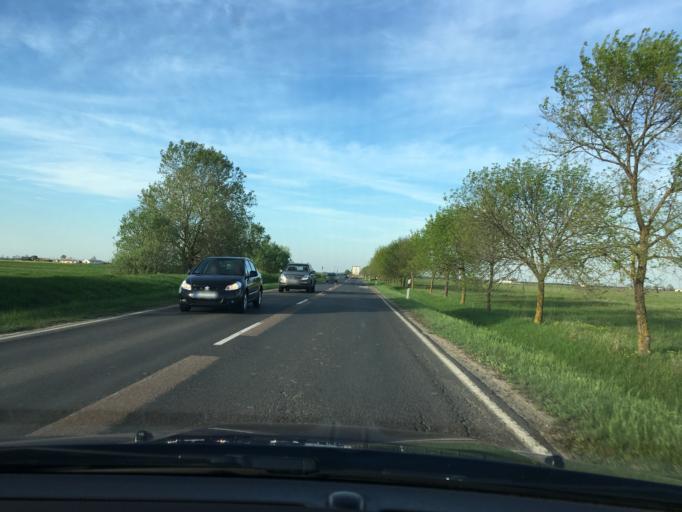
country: HU
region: Hajdu-Bihar
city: Berettyoujfalu
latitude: 47.1458
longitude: 21.4894
